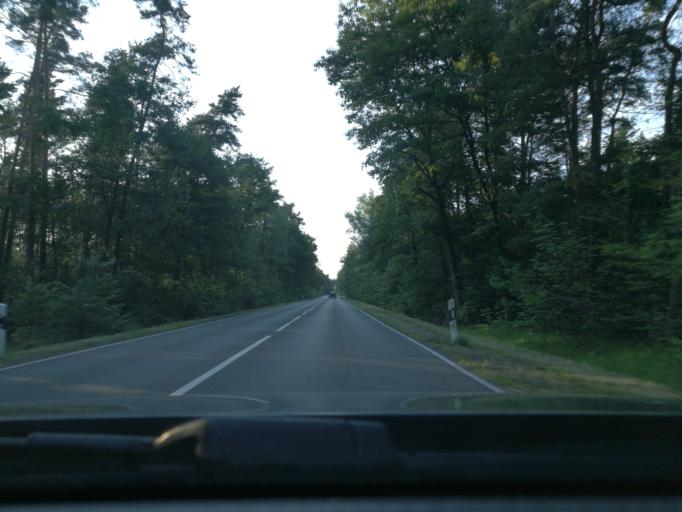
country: DE
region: Bavaria
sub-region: Regierungsbezirk Mittelfranken
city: Buckenhof
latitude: 49.5622
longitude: 11.0334
